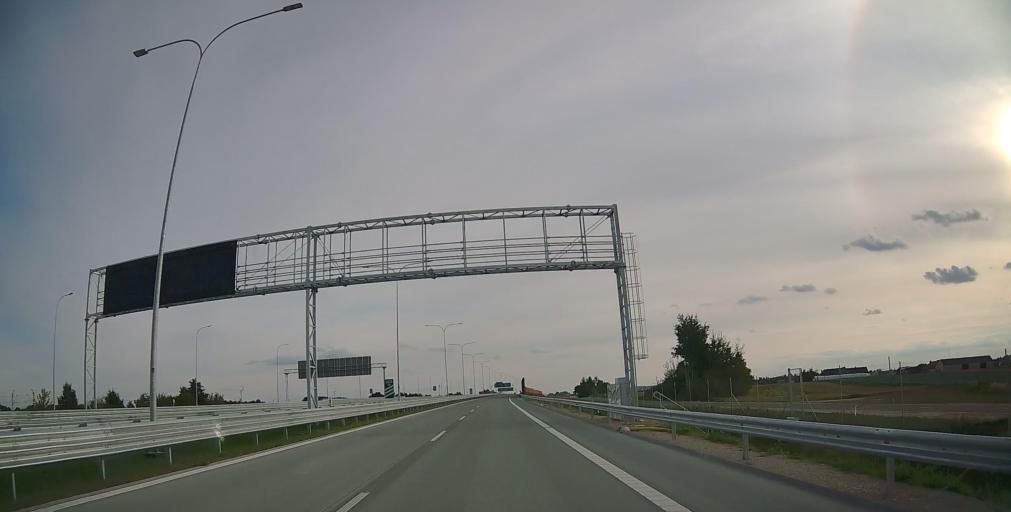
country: PL
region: Masovian Voivodeship
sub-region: Powiat piaseczynski
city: Mysiadlo
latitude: 52.1327
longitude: 20.9894
